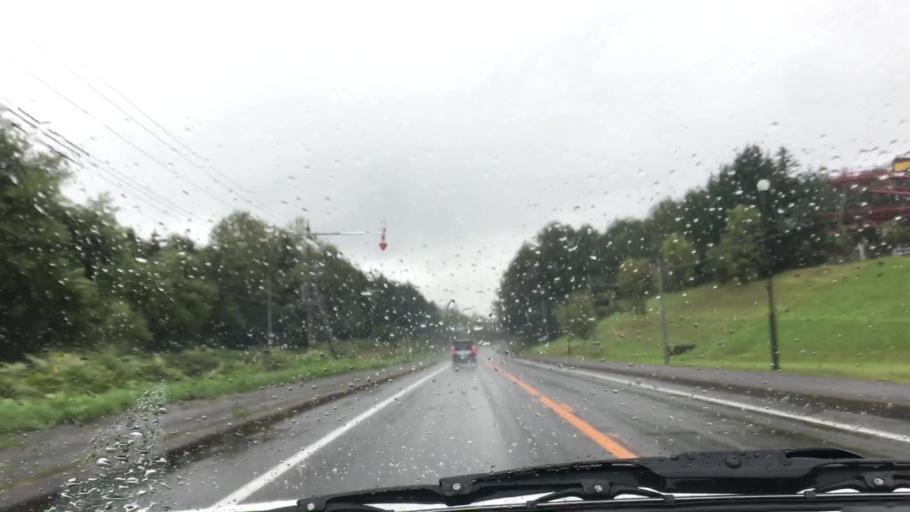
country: JP
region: Hokkaido
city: Niseko Town
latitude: 42.7463
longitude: 140.8970
